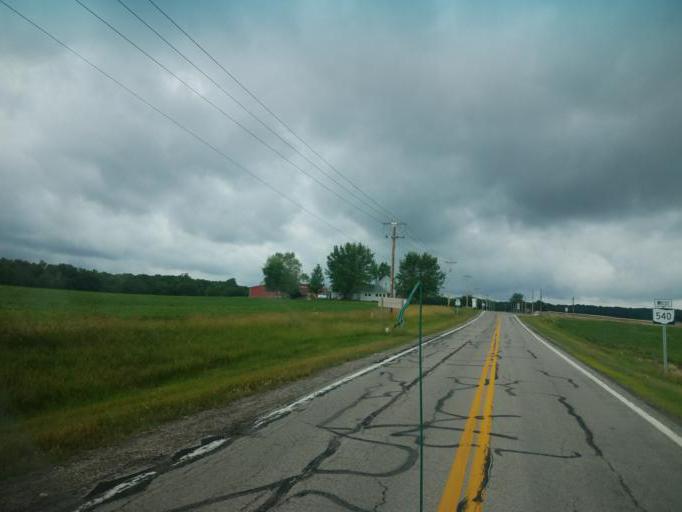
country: US
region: Ohio
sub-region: Logan County
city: Northwood
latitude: 40.3836
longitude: -83.6047
